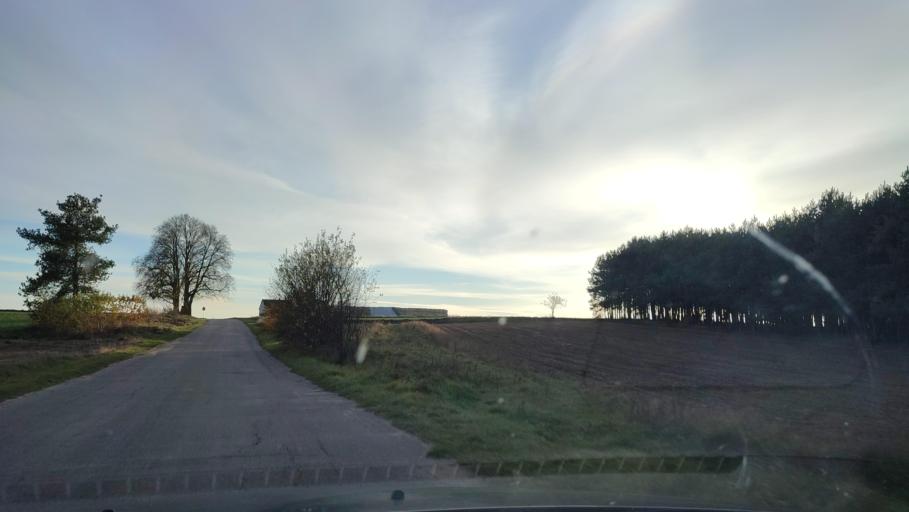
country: PL
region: Masovian Voivodeship
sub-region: Powiat mlawski
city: Dzierzgowo
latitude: 53.2721
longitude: 20.6457
